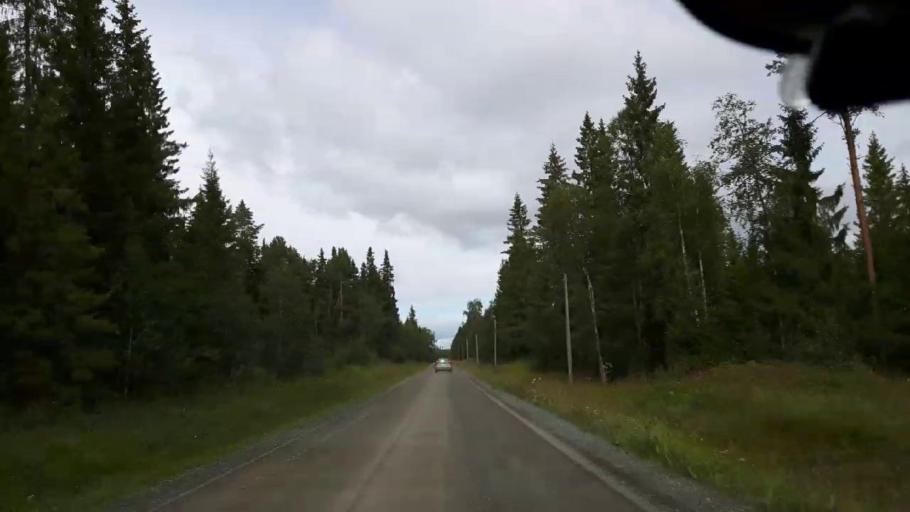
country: SE
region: Jaemtland
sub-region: Krokoms Kommun
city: Valla
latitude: 63.3961
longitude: 14.1005
